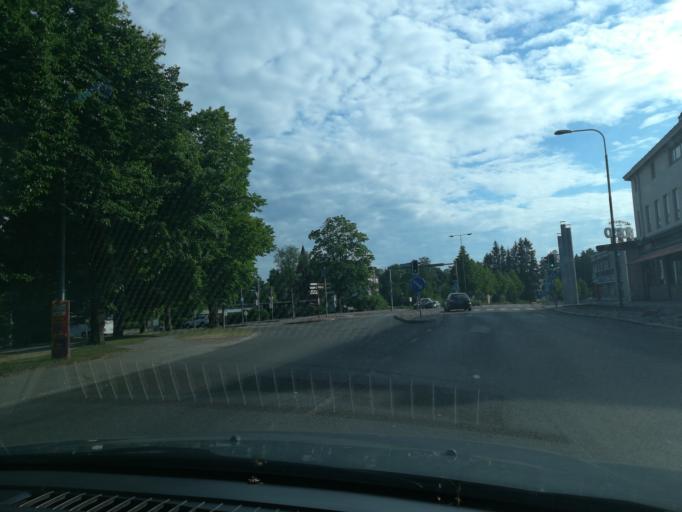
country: FI
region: South Karelia
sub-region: Imatra
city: Imatra
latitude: 61.1709
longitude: 28.7726
